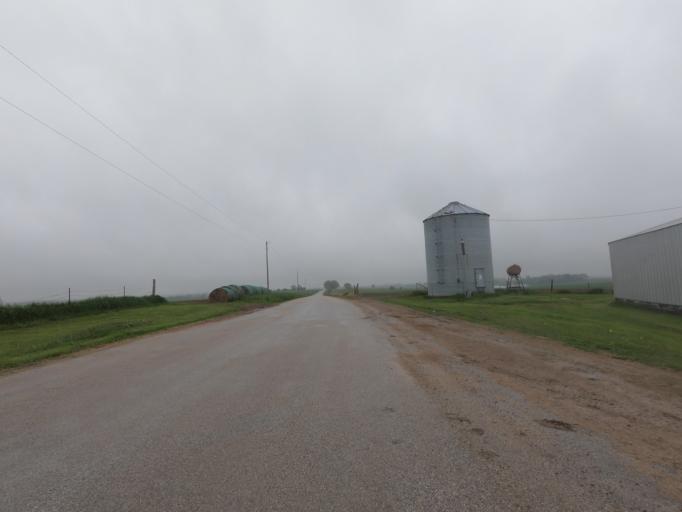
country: US
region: Wisconsin
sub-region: Grant County
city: Hazel Green
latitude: 42.5064
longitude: -90.5104
